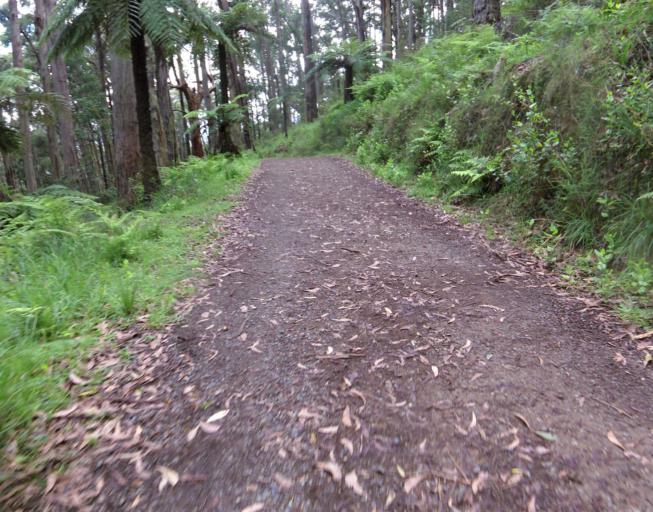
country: AU
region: Victoria
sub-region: Yarra Ranges
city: Montrose
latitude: -37.8386
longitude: 145.3436
